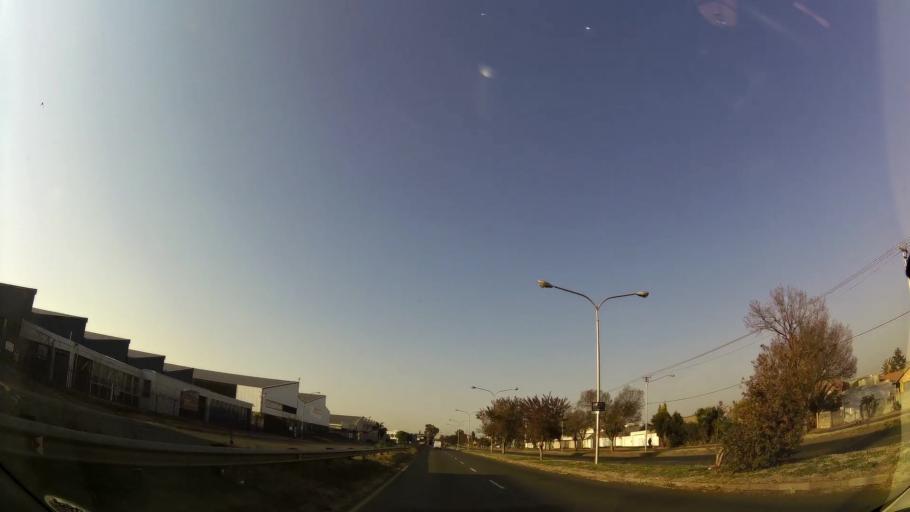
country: ZA
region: Gauteng
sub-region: City of Johannesburg Metropolitan Municipality
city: Modderfontein
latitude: -26.1466
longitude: 28.2000
